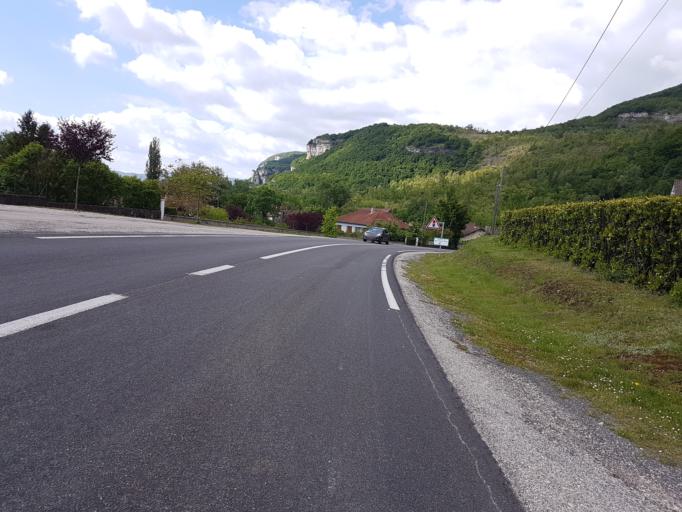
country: FR
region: Rhone-Alpes
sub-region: Departement de l'Isere
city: Bouvesse-Quirieu
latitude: 45.7926
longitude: 5.4609
